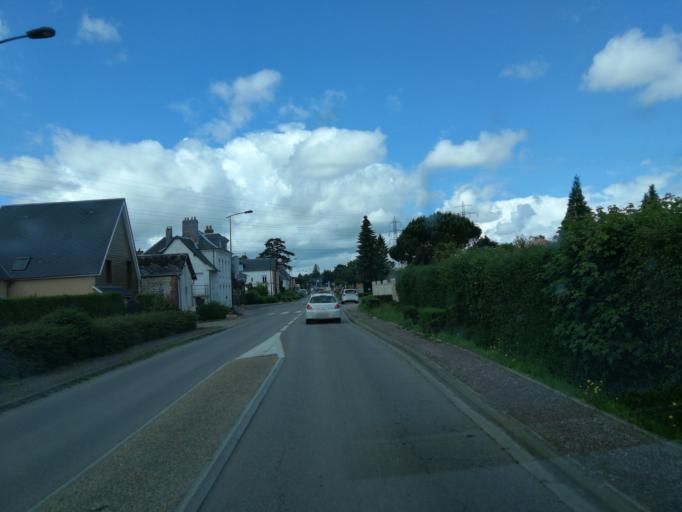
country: FR
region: Haute-Normandie
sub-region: Departement de l'Eure
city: Caumont
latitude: 49.3532
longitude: 0.9131
